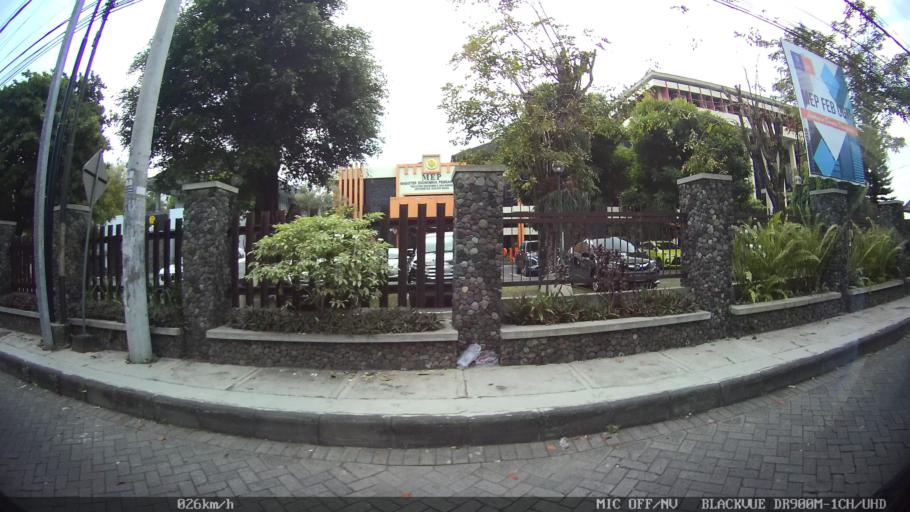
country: ID
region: Daerah Istimewa Yogyakarta
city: Yogyakarta
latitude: -7.7652
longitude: 110.3774
